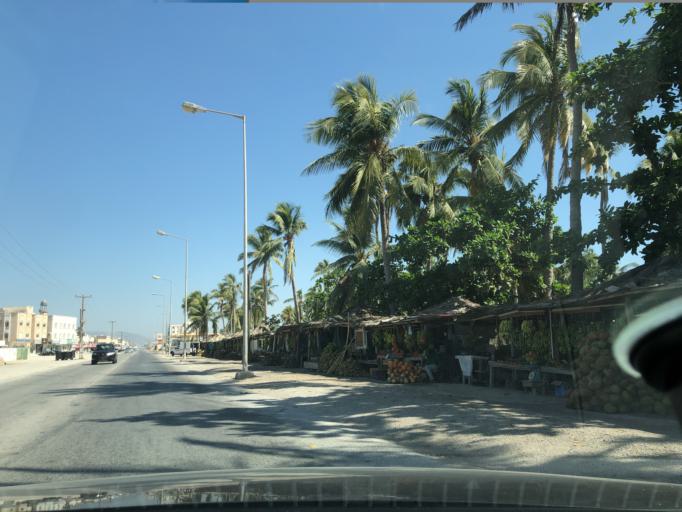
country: OM
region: Zufar
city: Salalah
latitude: 17.0183
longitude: 54.1580
